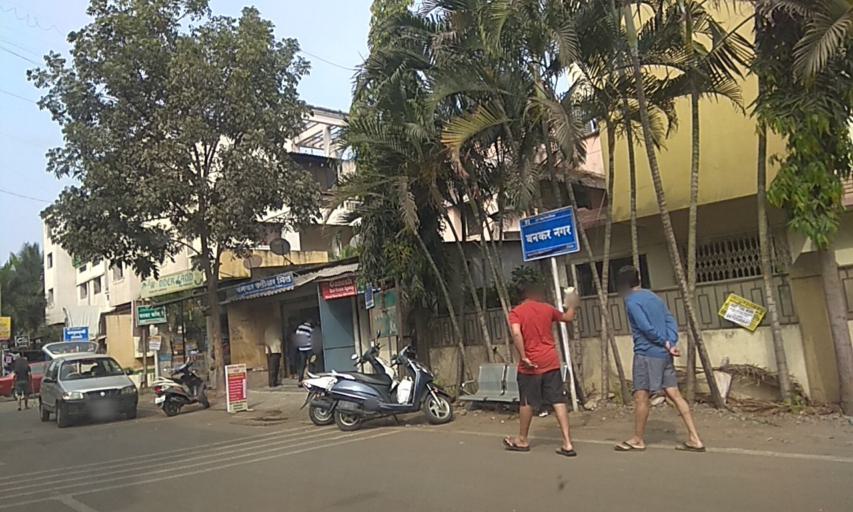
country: IN
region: Maharashtra
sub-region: Pune Division
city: Pune
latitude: 18.5042
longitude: 73.9317
